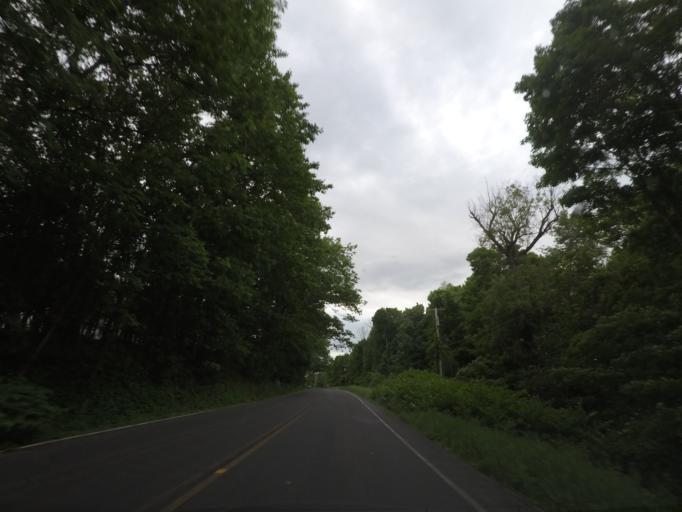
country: US
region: New York
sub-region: Dutchess County
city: Pine Plains
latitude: 41.9662
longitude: -73.5533
